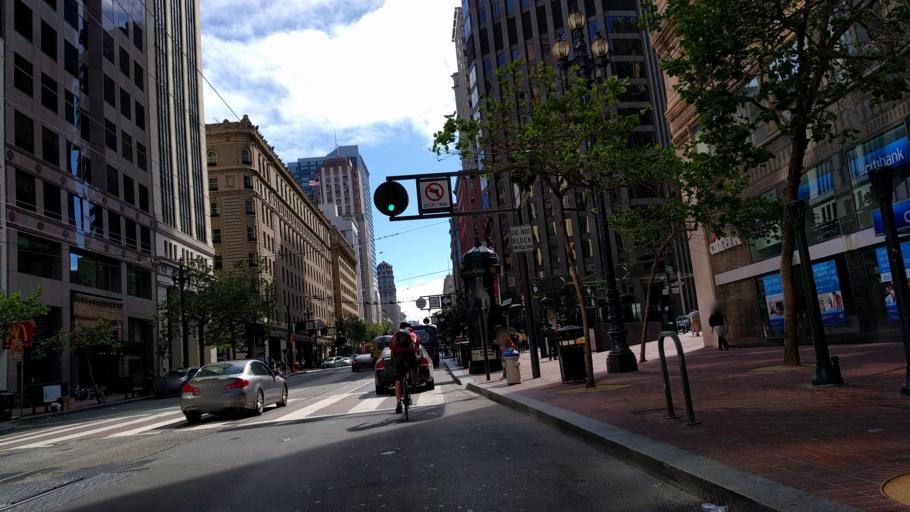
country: US
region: California
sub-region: San Francisco County
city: San Francisco
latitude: 37.7894
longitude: -122.4014
